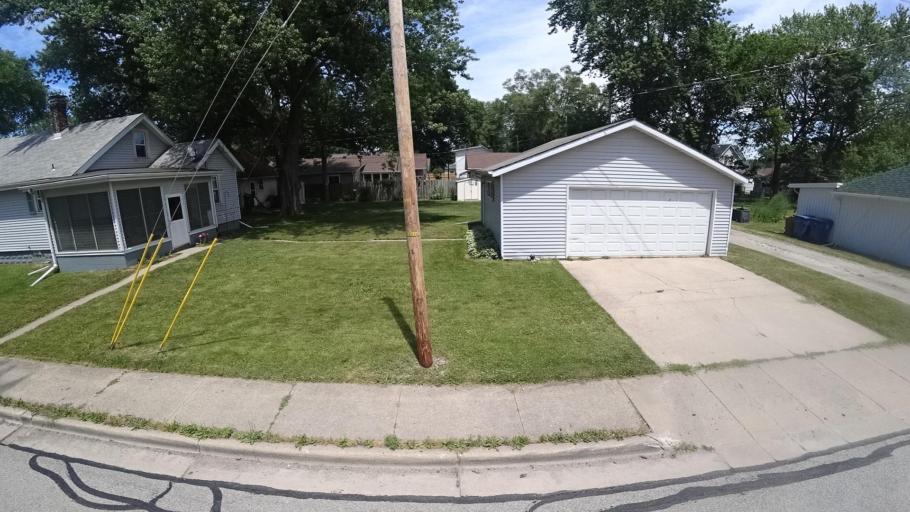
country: US
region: Indiana
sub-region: Porter County
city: Porter
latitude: 41.6168
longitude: -87.0751
